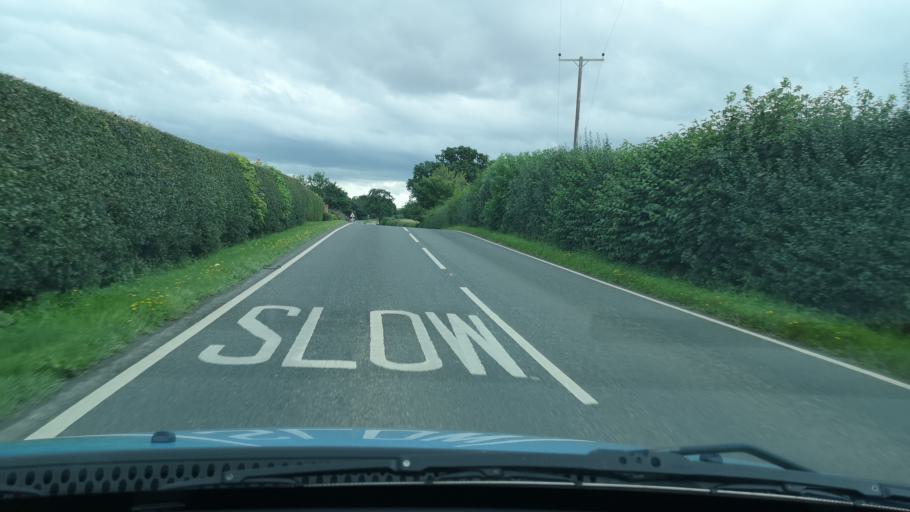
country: GB
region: England
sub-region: City and Borough of Wakefield
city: Featherstone
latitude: 53.6591
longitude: -1.3573
